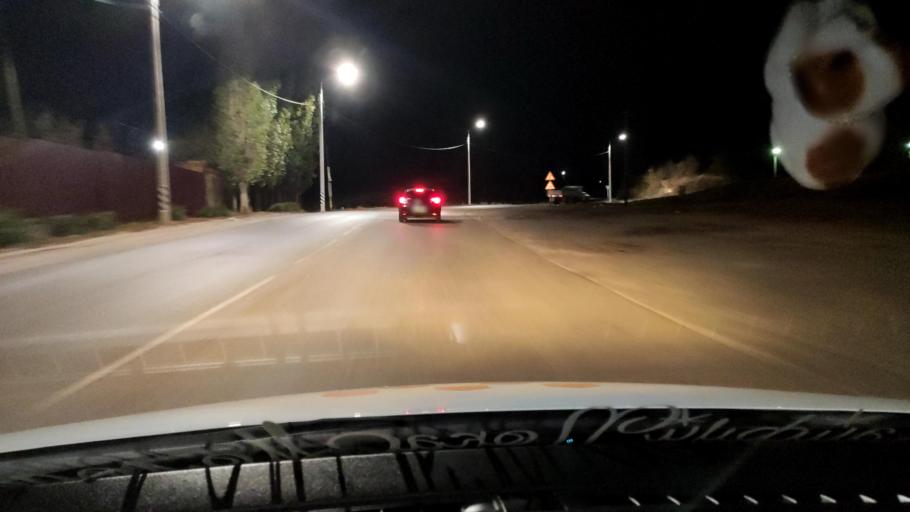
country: RU
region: Voronezj
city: Semiluki
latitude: 51.6798
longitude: 39.0246
